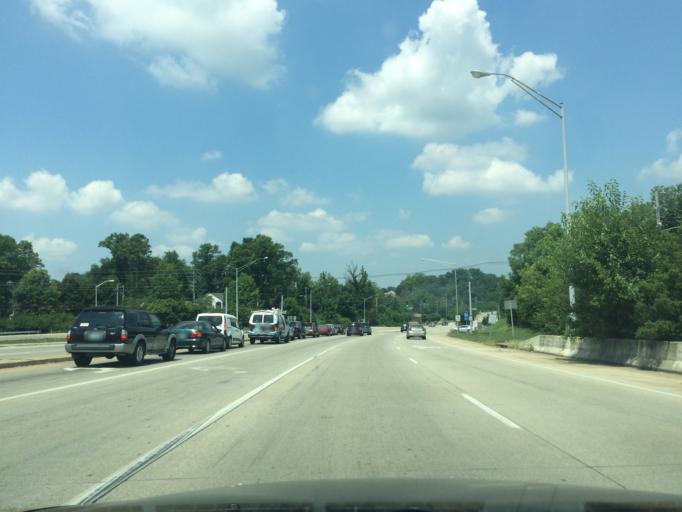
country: US
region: Kentucky
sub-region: Jefferson County
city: West Buechel
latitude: 38.2024
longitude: -85.6899
